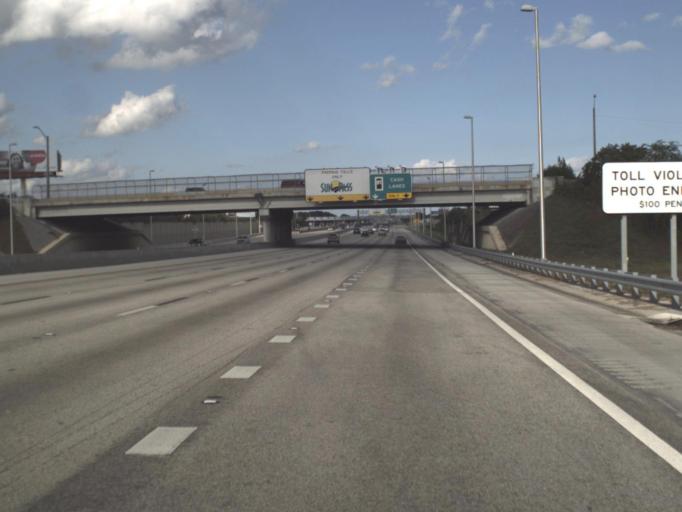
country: US
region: Florida
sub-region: Broward County
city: Palm Aire
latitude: 26.2029
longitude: -80.2015
